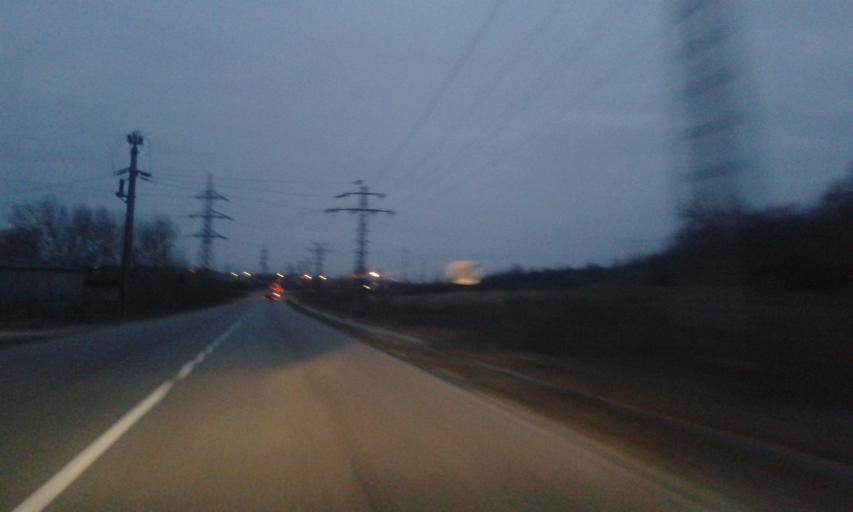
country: RO
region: Gorj
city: Targu Jiu
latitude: 45.0574
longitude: 23.2661
